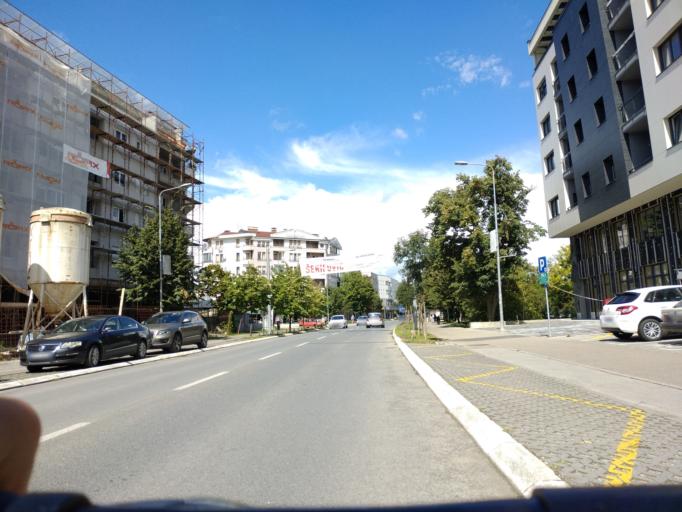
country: BA
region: Republika Srpska
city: Mejdan - Obilicevo
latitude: 44.7680
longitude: 17.1991
